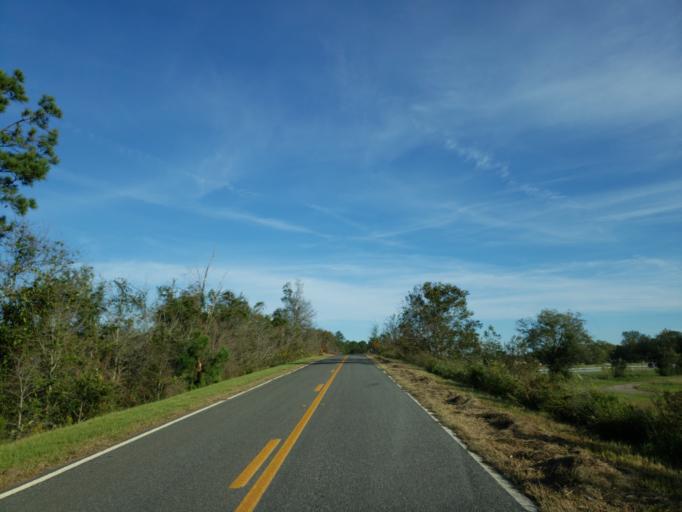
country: US
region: Georgia
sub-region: Dooly County
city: Vienna
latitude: 32.0609
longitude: -83.7659
